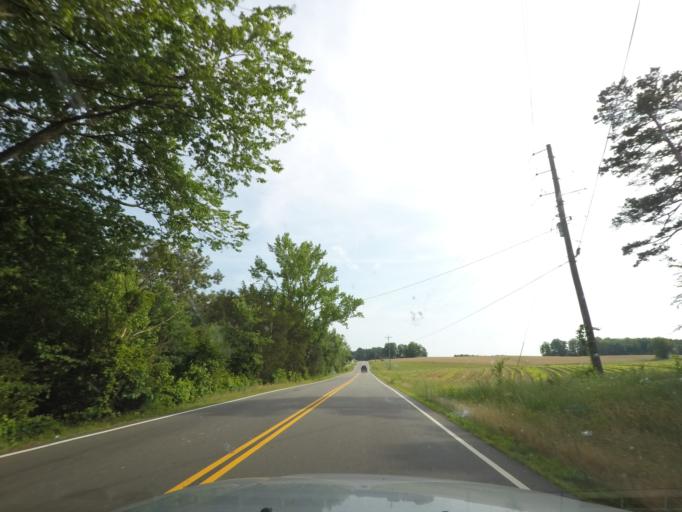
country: US
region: Virginia
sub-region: Mecklenburg County
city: Chase City
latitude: 36.8515
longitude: -78.5934
